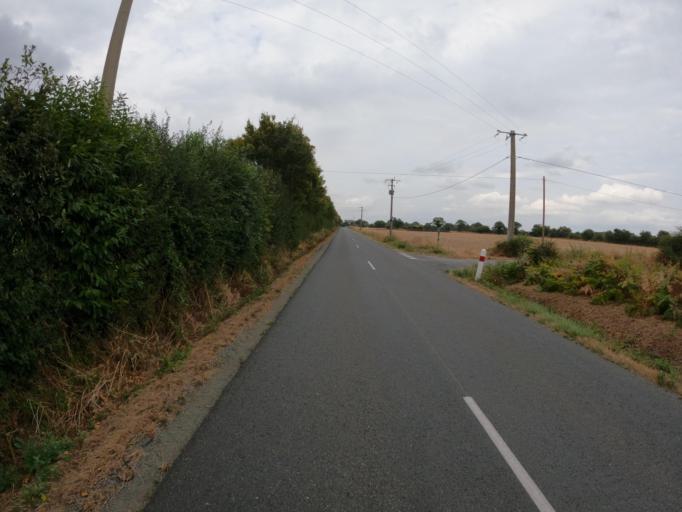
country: FR
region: Pays de la Loire
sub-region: Departement de Maine-et-Loire
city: La Romagne
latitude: 47.0503
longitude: -1.0311
